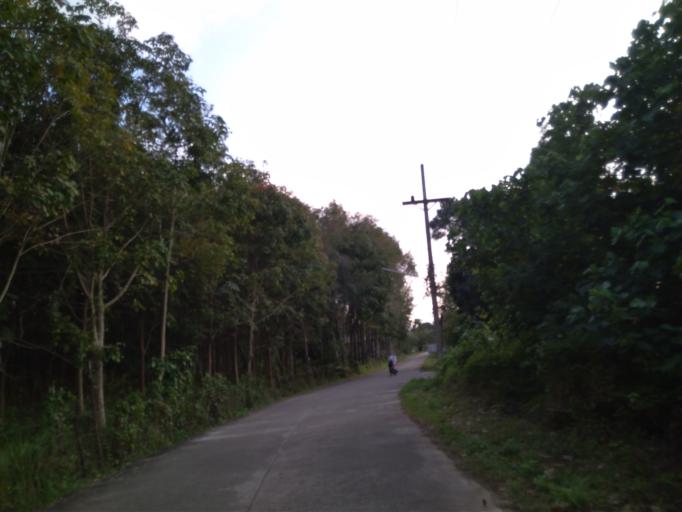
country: TH
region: Phangnga
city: Ko Yao
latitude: 8.1417
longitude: 98.5989
